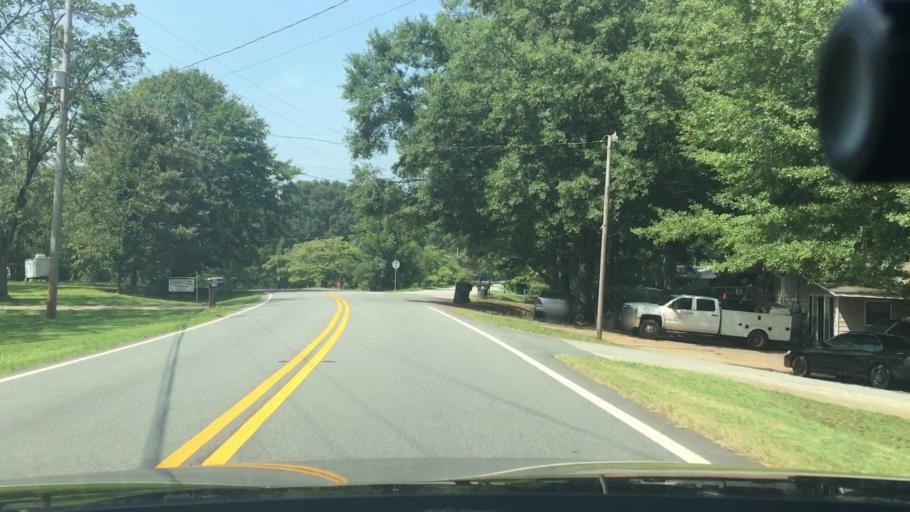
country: US
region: Georgia
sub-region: Coweta County
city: East Newnan
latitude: 33.3568
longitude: -84.7711
